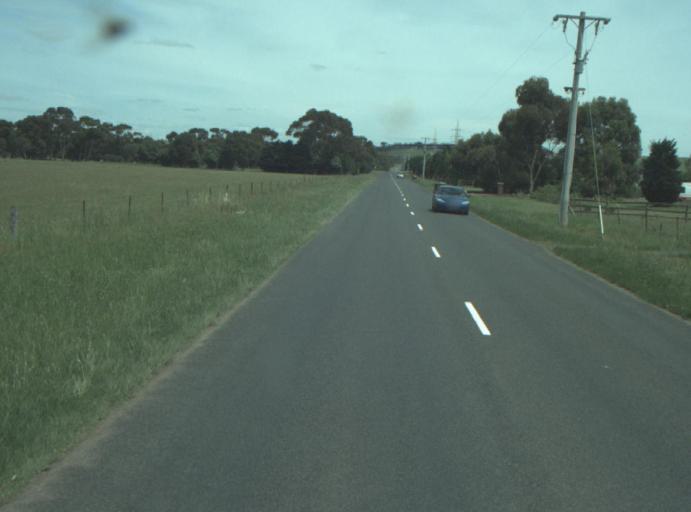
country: AU
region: Victoria
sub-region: Greater Geelong
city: Lara
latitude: -38.0230
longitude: 144.3720
